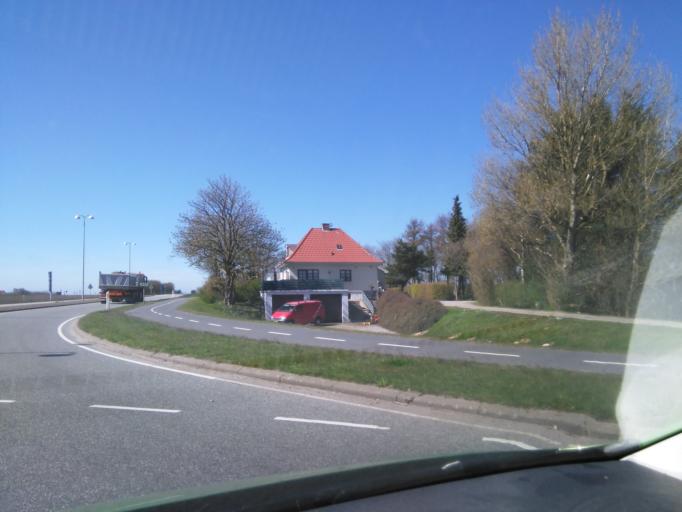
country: DK
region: South Denmark
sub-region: Varde Kommune
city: Oksbol
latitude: 55.6179
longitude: 8.3258
